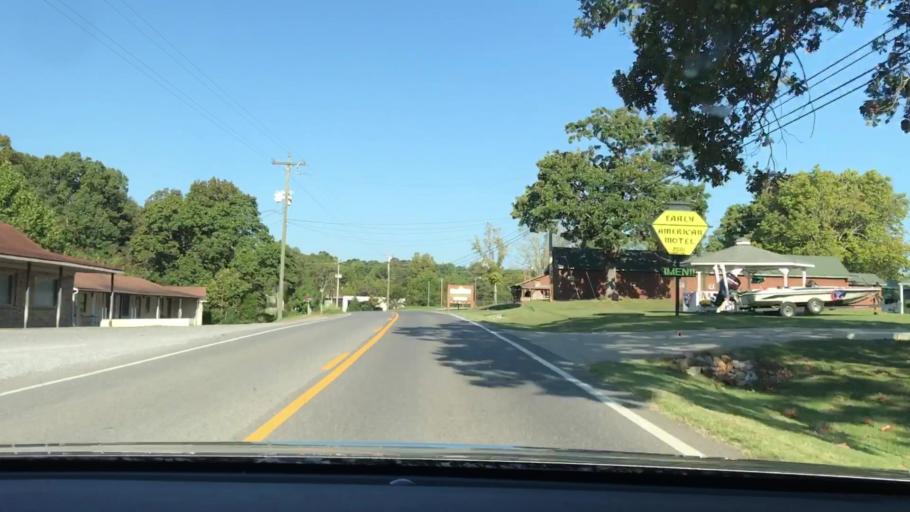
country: US
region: Kentucky
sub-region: Marshall County
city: Benton
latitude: 36.7762
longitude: -88.1437
